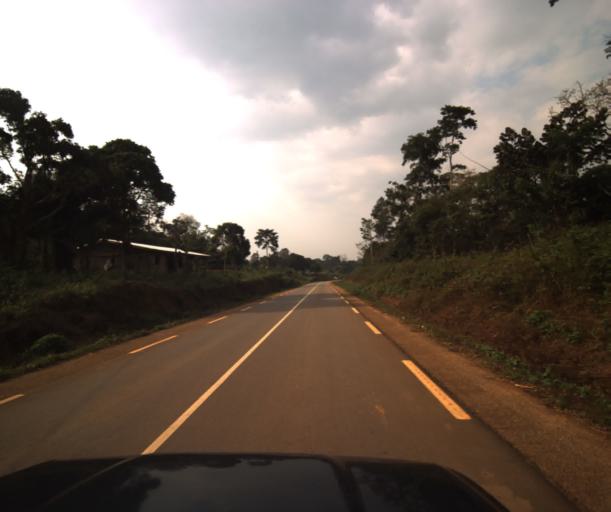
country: CM
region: Centre
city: Mbankomo
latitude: 3.7608
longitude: 11.4059
